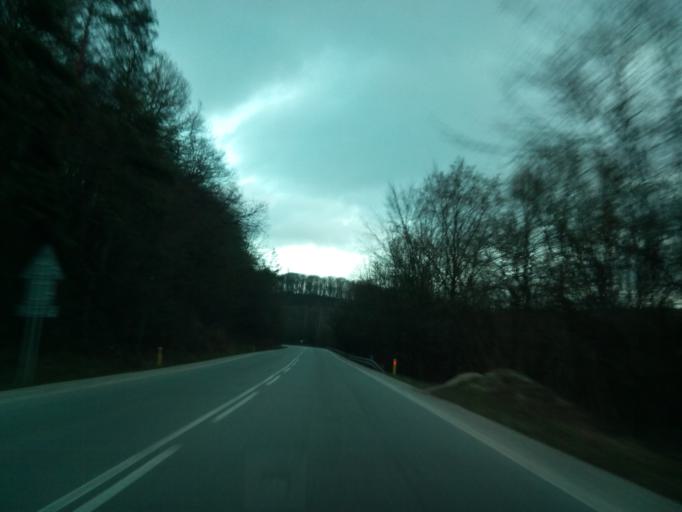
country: SK
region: Kosicky
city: Roznava
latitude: 48.6239
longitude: 20.6316
